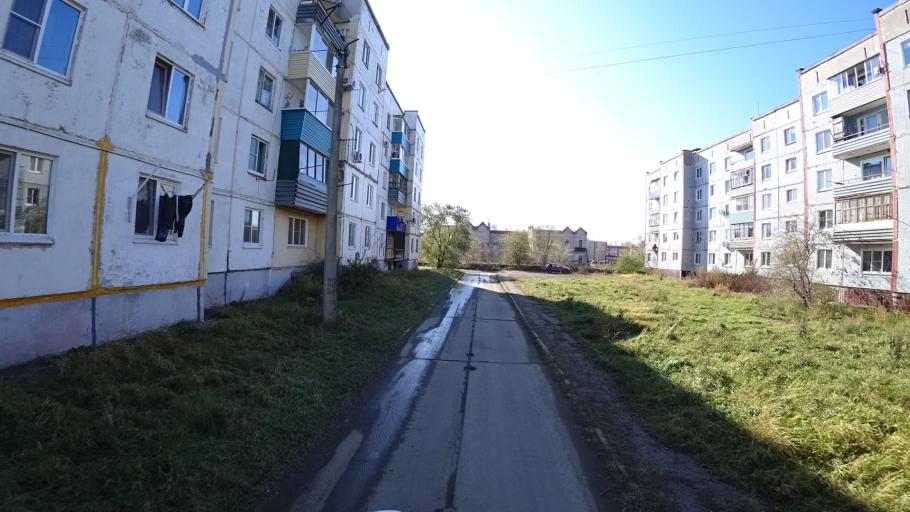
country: RU
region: Khabarovsk Krai
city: Amursk
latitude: 50.1040
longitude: 136.5185
